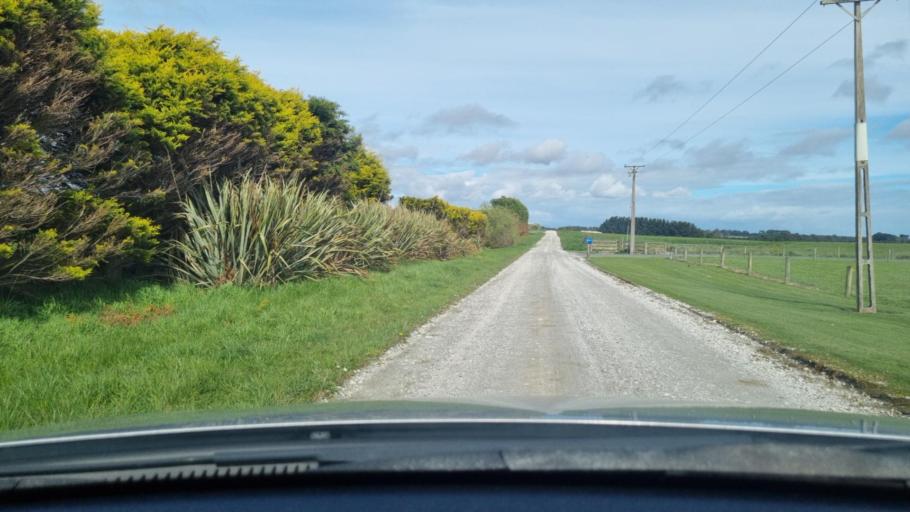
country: NZ
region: Southland
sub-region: Invercargill City
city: Invercargill
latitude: -46.4538
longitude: 168.3837
